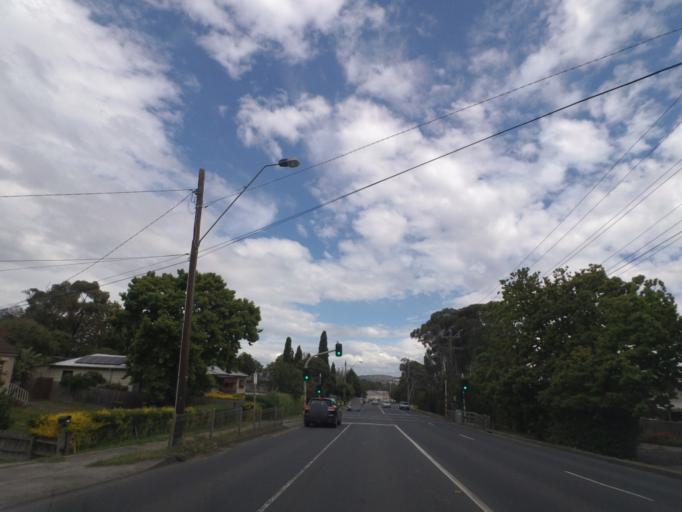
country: AU
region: Victoria
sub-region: Knox
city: Ferntree Gully
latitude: -37.8835
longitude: 145.2844
